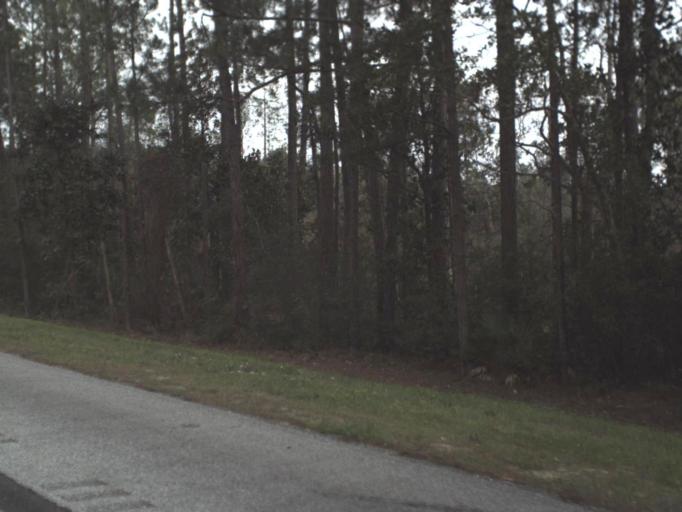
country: US
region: Florida
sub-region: Okaloosa County
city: Crestview
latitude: 30.7297
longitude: -86.3876
